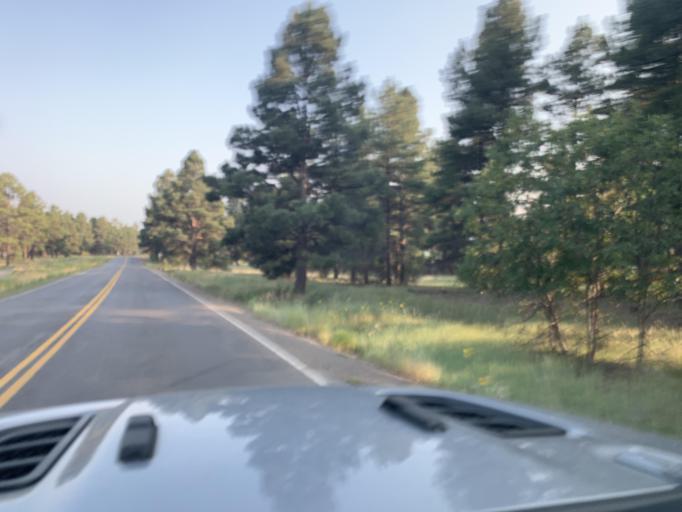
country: US
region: Colorado
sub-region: Archuleta County
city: Pagosa Springs
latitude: 37.2666
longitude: -107.0958
